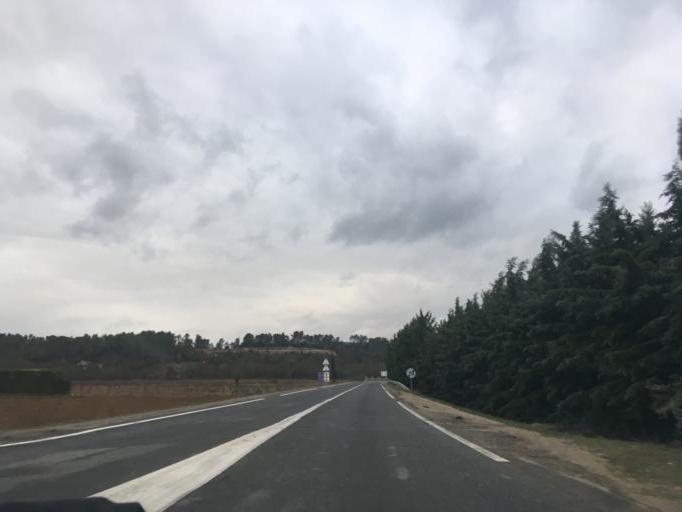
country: FR
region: Provence-Alpes-Cote d'Azur
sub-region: Departement du Var
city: Besse-sur-Issole
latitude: 43.3481
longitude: 6.1815
